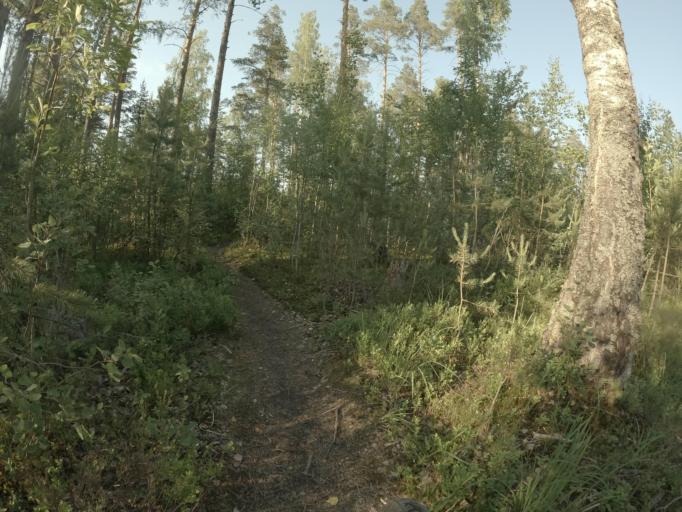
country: RU
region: Leningrad
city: Yakovlevo
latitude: 60.4377
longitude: 29.2385
